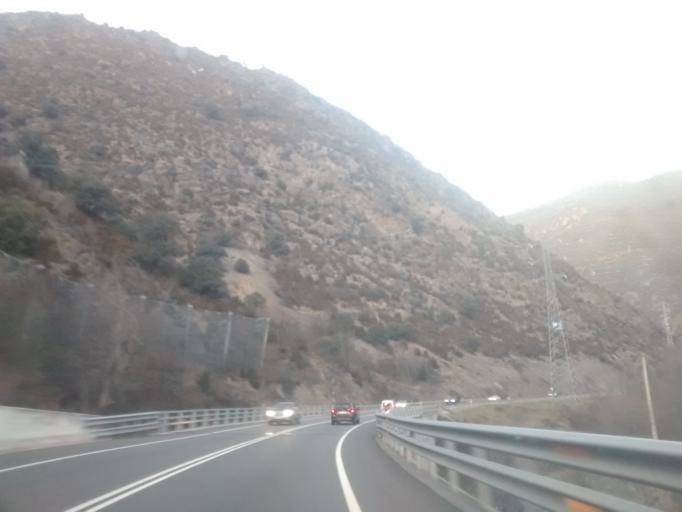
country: ES
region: Catalonia
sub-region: Provincia de Lleida
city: la Seu d'Urgell
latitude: 42.4020
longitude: 1.4625
